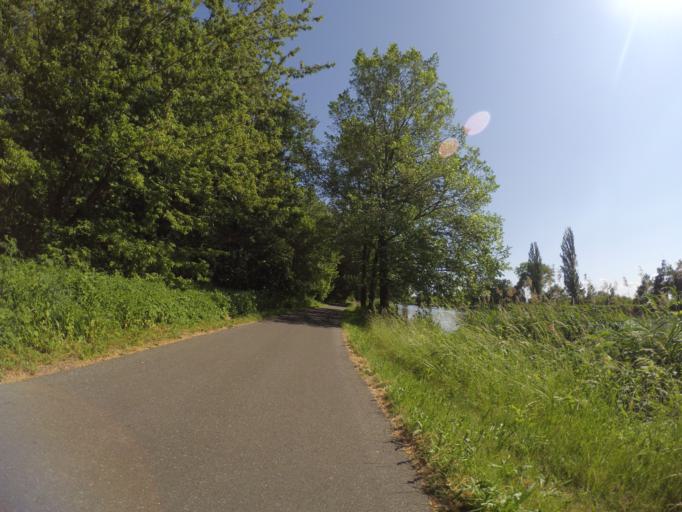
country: CZ
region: Central Bohemia
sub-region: Okres Nymburk
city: Nymburk
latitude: 50.1757
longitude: 15.0763
